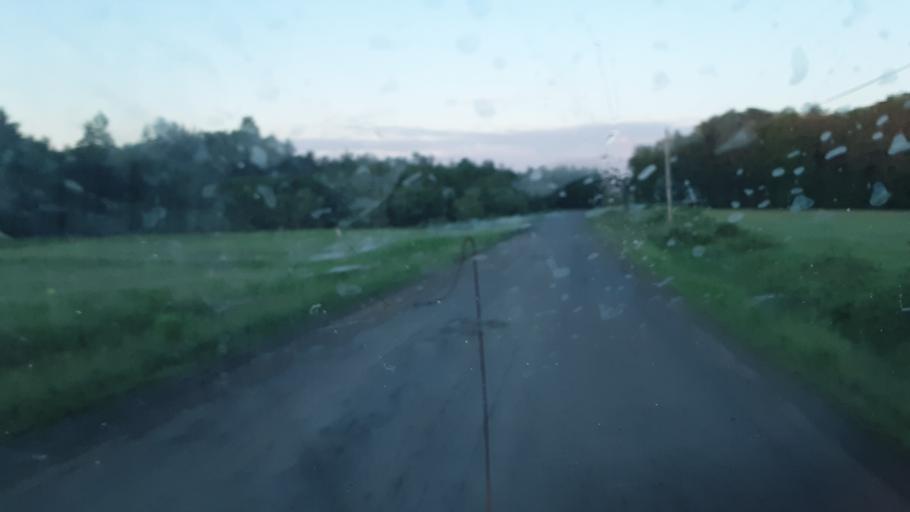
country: US
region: Maine
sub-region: Aroostook County
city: Caribou
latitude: 46.8733
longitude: -68.1205
